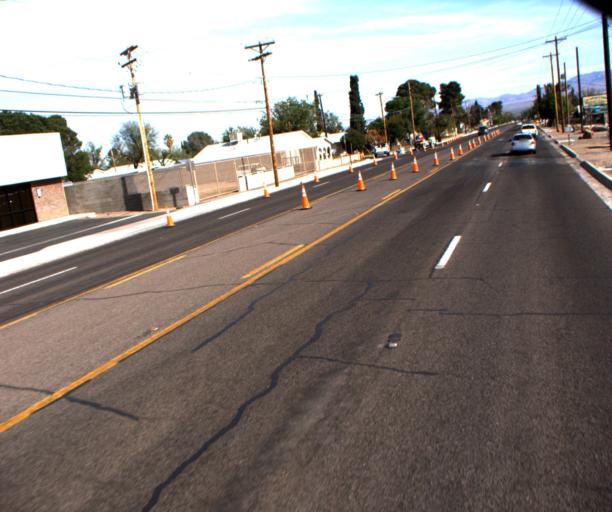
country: US
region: Arizona
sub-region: Graham County
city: Safford
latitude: 32.8204
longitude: -109.7076
